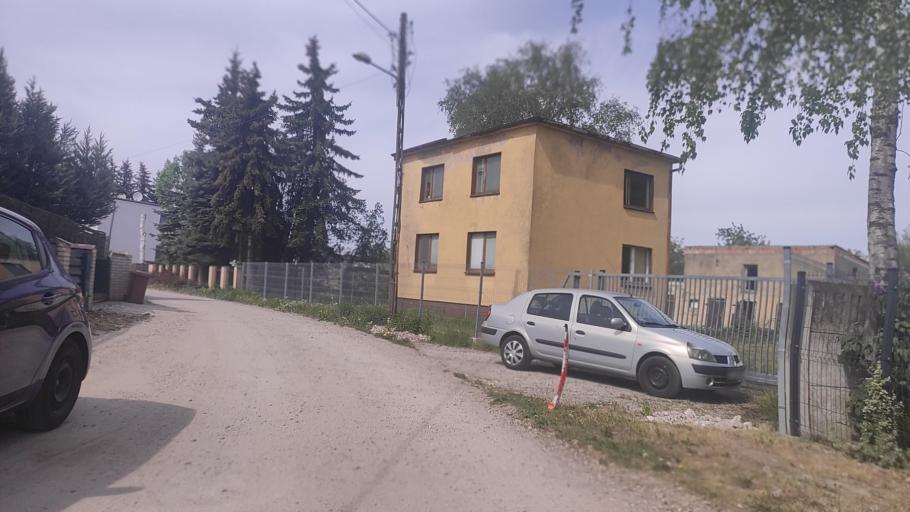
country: PL
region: Greater Poland Voivodeship
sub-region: Powiat poznanski
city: Swarzedz
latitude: 52.4081
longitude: 17.1060
